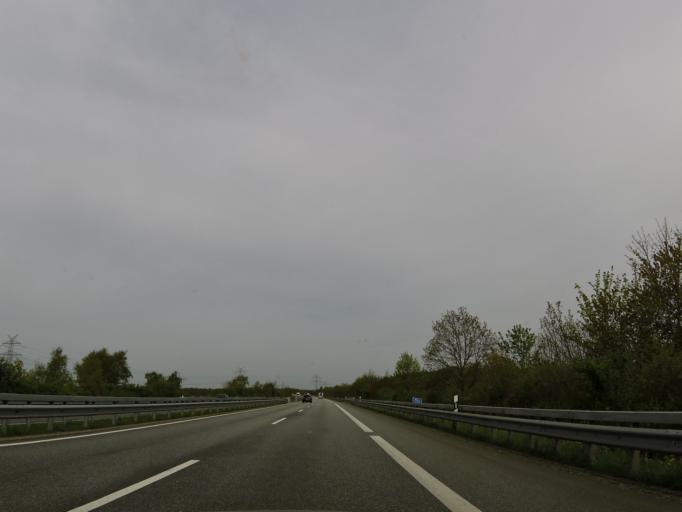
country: DE
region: Schleswig-Holstein
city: Kaaks
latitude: 53.9924
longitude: 9.4882
